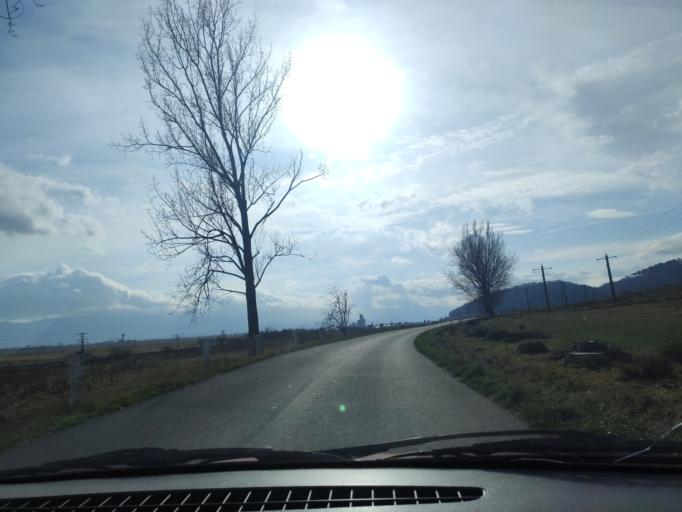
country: RO
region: Brasov
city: Codlea
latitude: 45.7294
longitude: 25.4575
